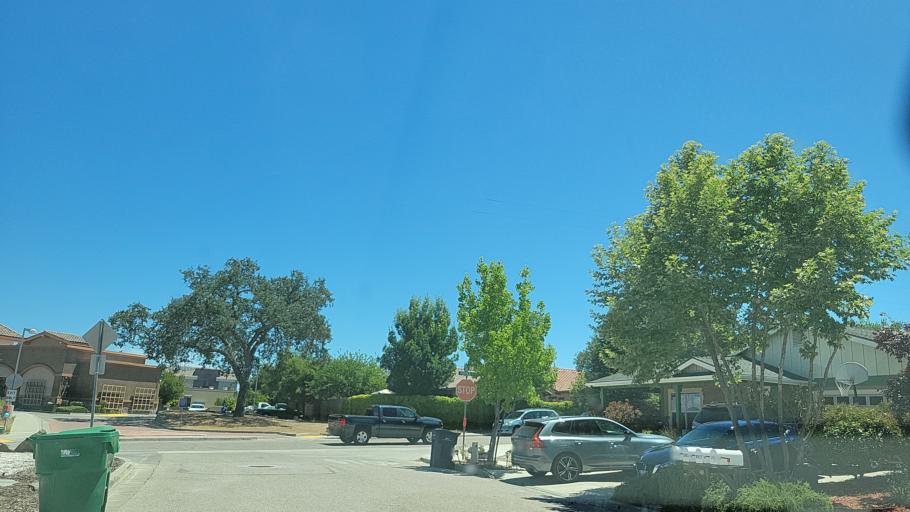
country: US
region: California
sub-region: San Luis Obispo County
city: Atascadero
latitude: 35.4688
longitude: -120.6547
